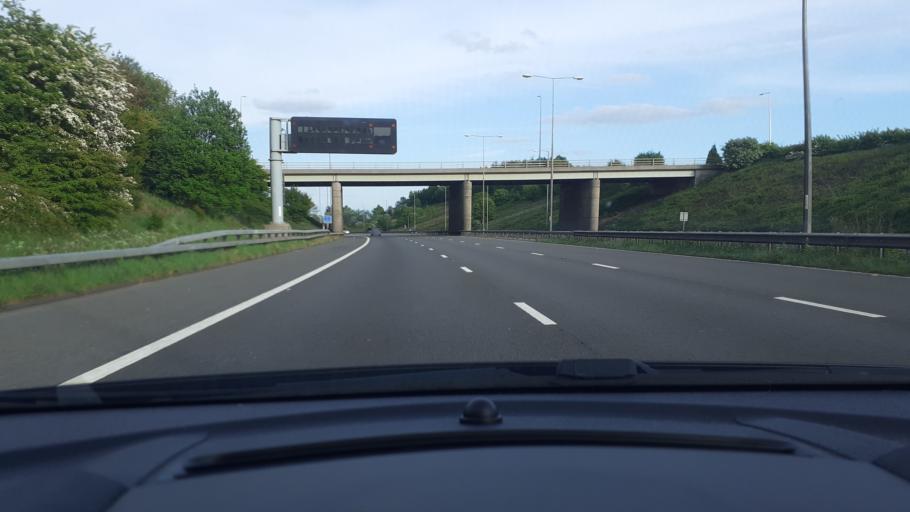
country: GB
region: England
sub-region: St. Helens
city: Billinge
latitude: 53.5139
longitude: -2.6891
